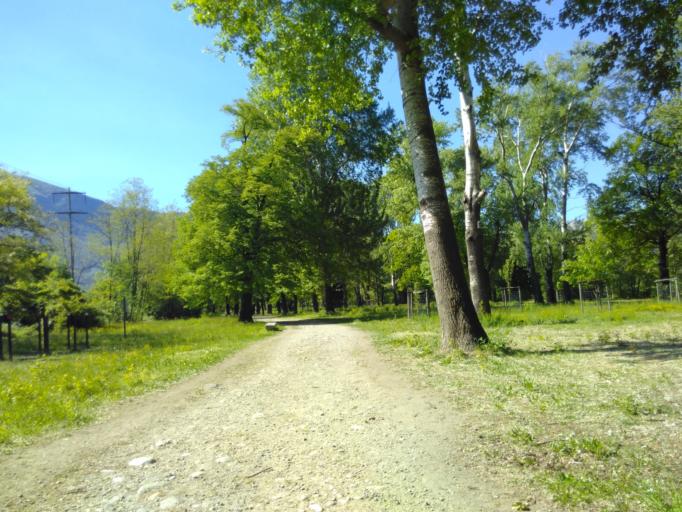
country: CH
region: Ticino
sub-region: Bellinzona District
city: Monte Carasso
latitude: 46.1893
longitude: 9.0080
